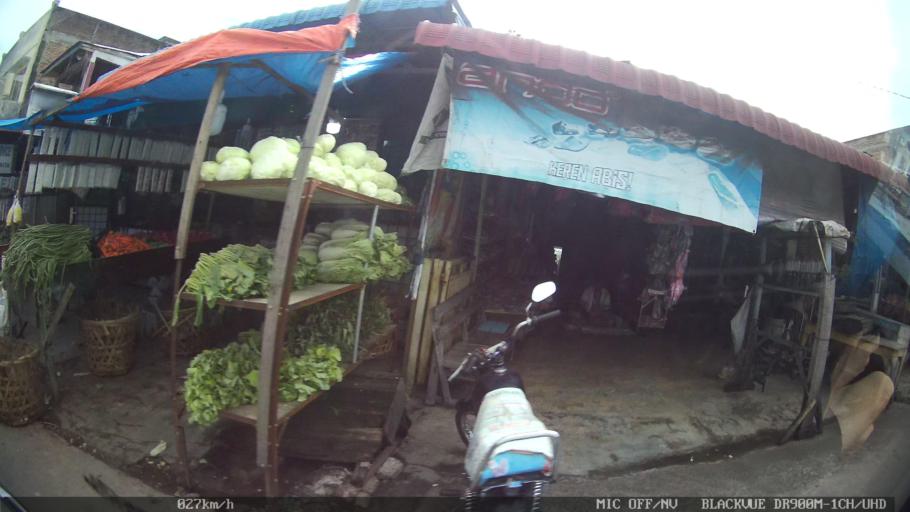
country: ID
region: North Sumatra
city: Percut
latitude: 3.6156
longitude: 98.7999
